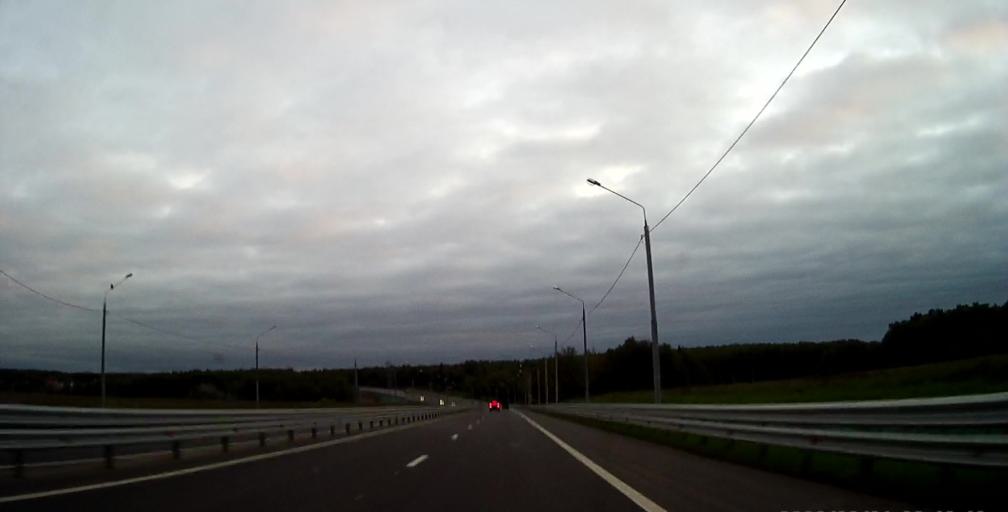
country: RU
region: Moskovskaya
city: Dubrovitsy
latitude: 55.4107
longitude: 37.5019
